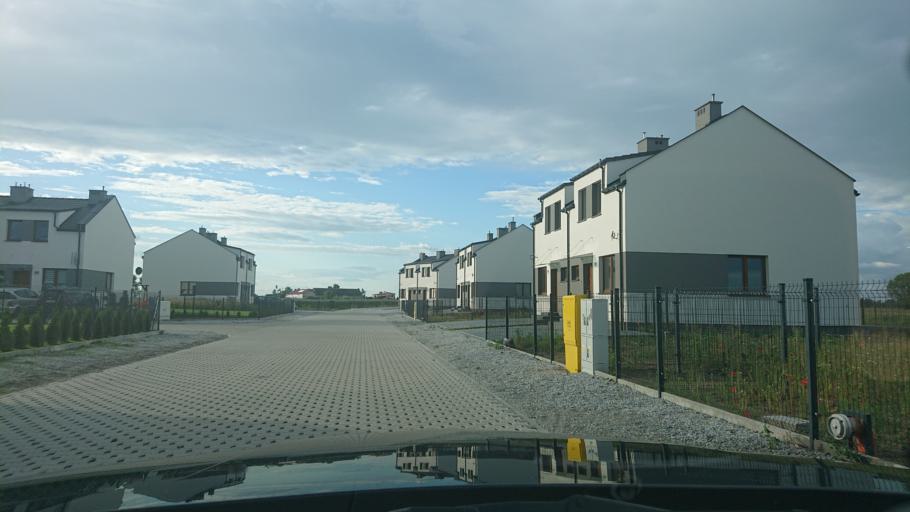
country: PL
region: Greater Poland Voivodeship
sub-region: Powiat gnieznienski
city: Gniezno
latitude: 52.5673
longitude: 17.6169
